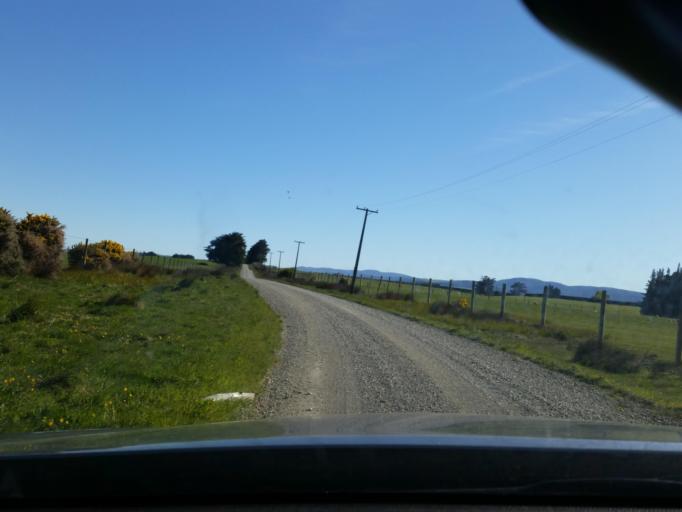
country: NZ
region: Southland
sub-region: Southland District
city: Winton
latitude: -46.2131
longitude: 168.4851
